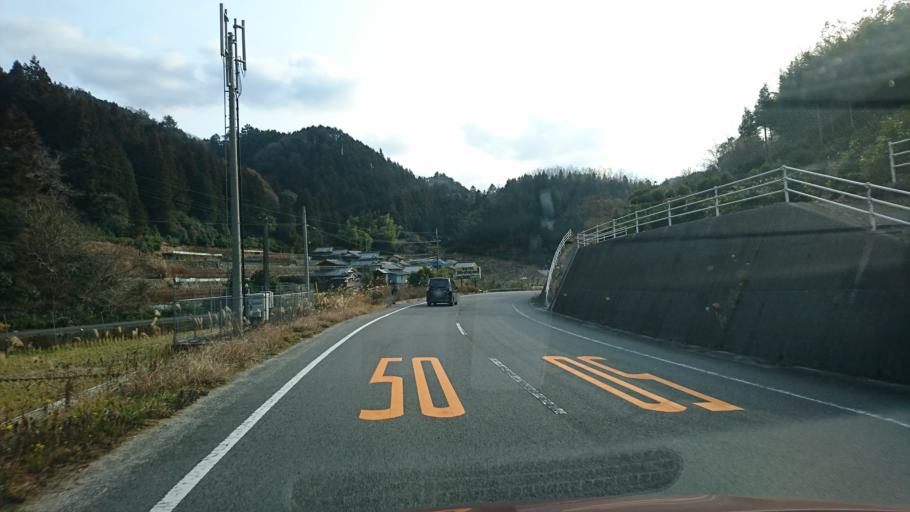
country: JP
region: Ehime
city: Hojo
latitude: 33.9194
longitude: 132.8859
